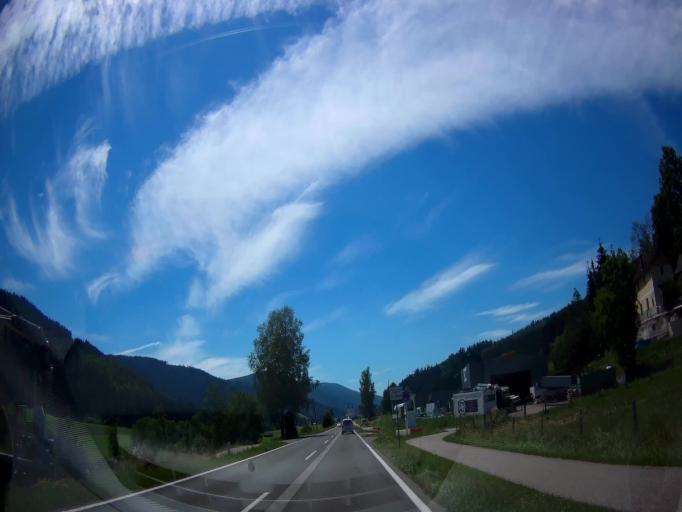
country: AT
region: Carinthia
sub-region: Politischer Bezirk Sankt Veit an der Glan
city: Gurk
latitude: 46.8836
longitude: 14.3102
